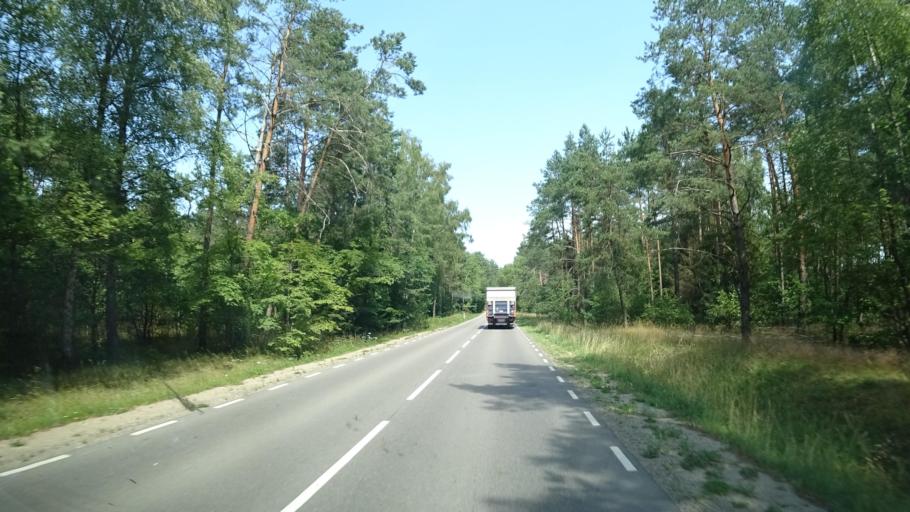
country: PL
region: Pomeranian Voivodeship
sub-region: Powiat koscierski
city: Lipusz
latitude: 54.0922
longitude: 17.8056
